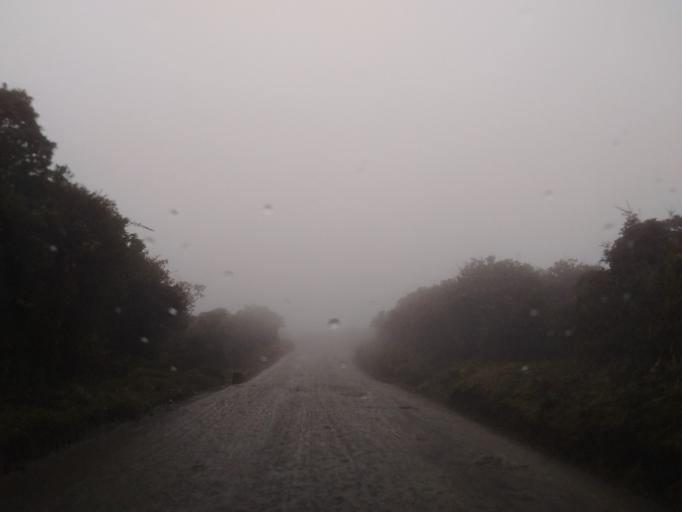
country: CO
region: Cauca
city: Paispamba
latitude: 2.1532
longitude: -76.4201
